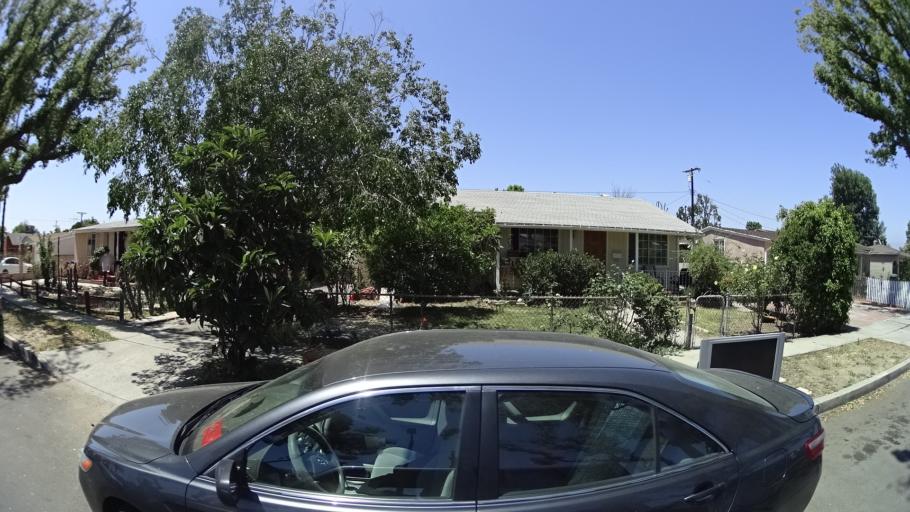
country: US
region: California
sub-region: Los Angeles County
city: Van Nuys
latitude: 34.2180
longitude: -118.4371
